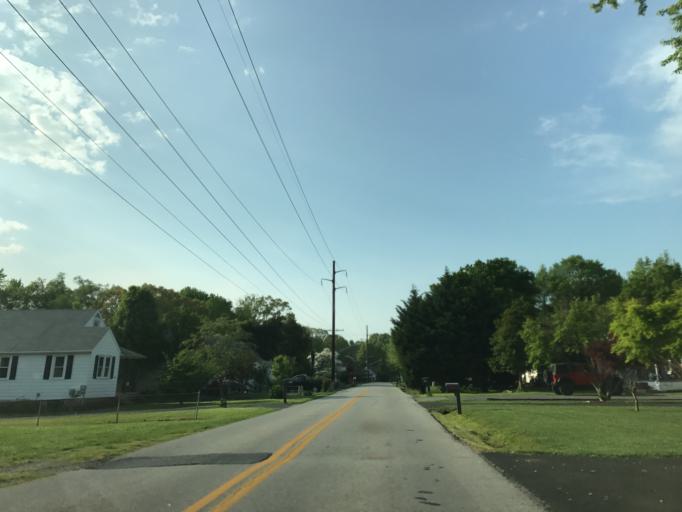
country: US
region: Maryland
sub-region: Baltimore County
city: Middle River
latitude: 39.3426
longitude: -76.4354
